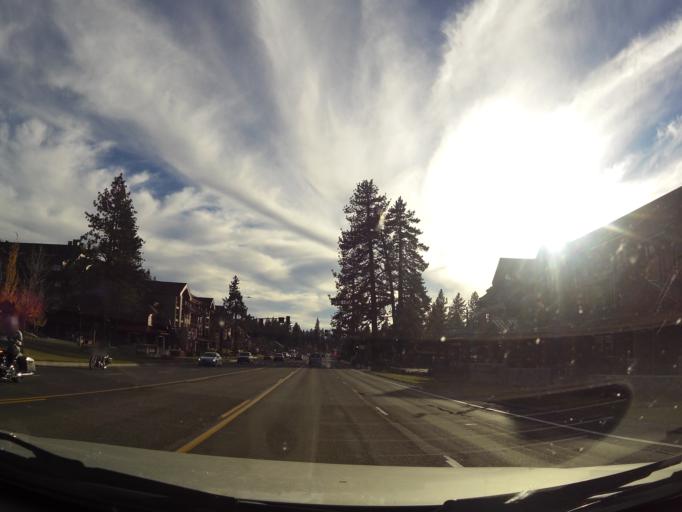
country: US
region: Nevada
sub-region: Douglas County
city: Kingsbury
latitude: 38.9577
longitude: -119.9432
